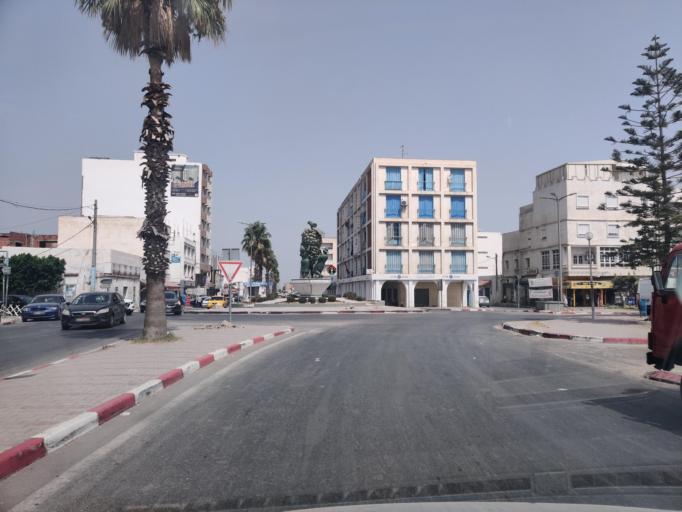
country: TN
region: Nabul
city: Bu `Urqub
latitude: 36.5981
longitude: 10.4993
